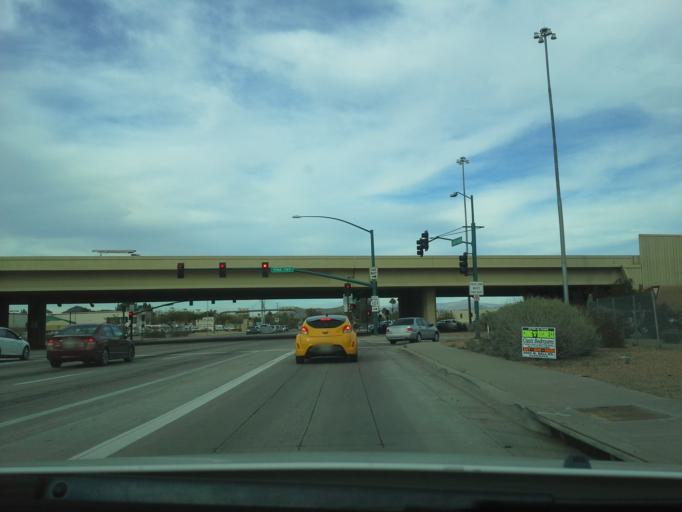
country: US
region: Arizona
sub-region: Maricopa County
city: Paradise Valley
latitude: 33.6714
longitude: -112.0309
